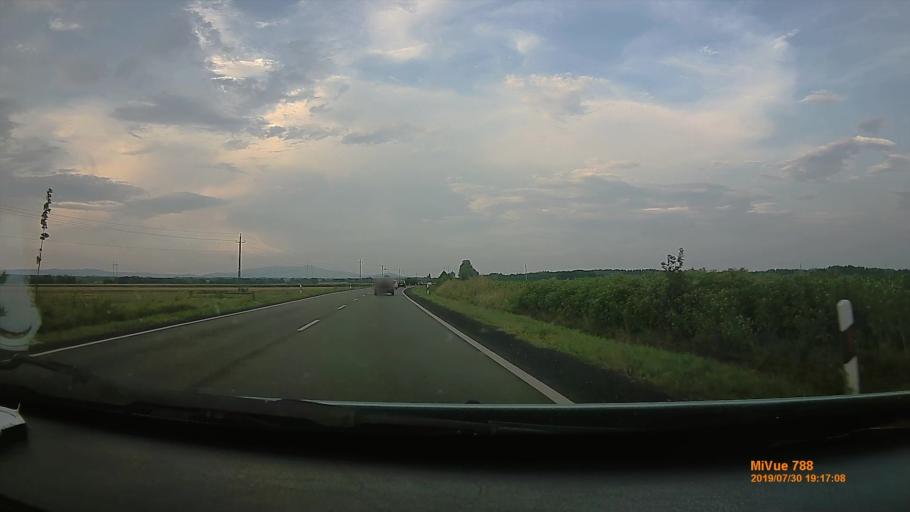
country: HU
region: Heves
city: Hort
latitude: 47.6956
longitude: 19.8023
